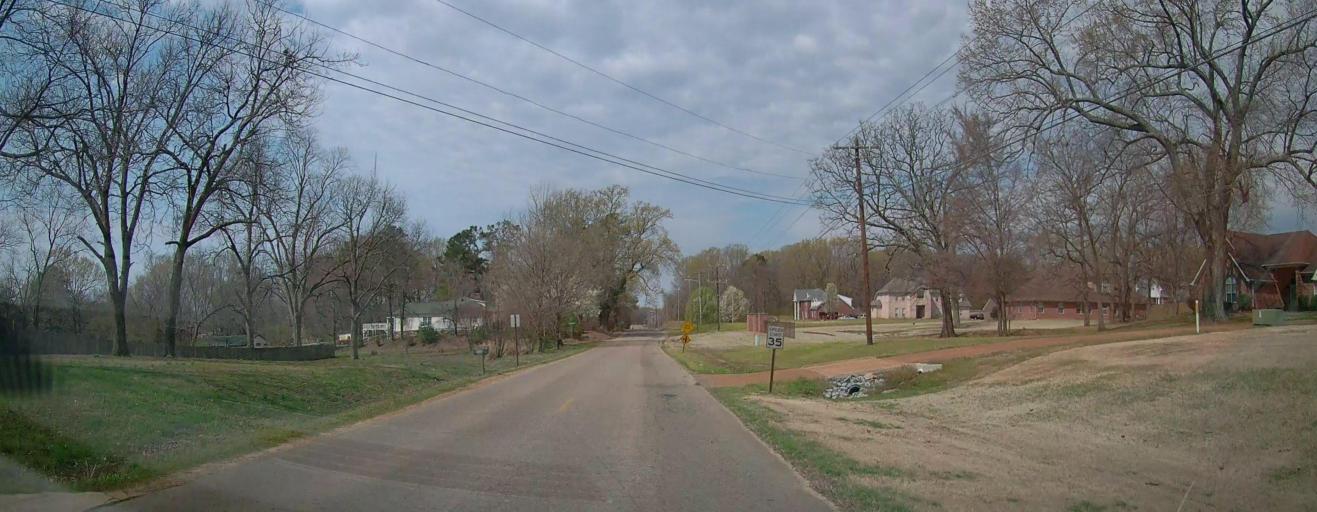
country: US
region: Mississippi
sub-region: De Soto County
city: Olive Branch
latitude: 34.9913
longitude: -89.8563
